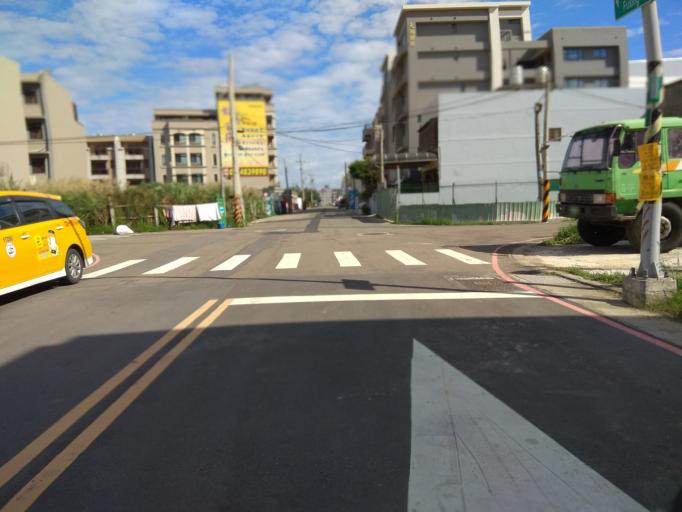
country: TW
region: Taiwan
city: Taoyuan City
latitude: 25.0425
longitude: 121.1350
